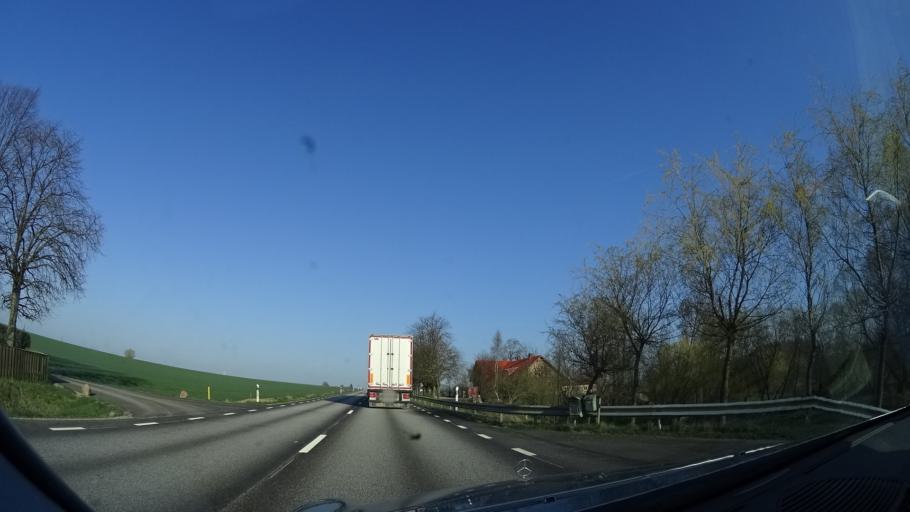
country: SE
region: Skane
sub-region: Eslovs Kommun
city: Eslov
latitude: 55.8568
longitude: 13.2677
